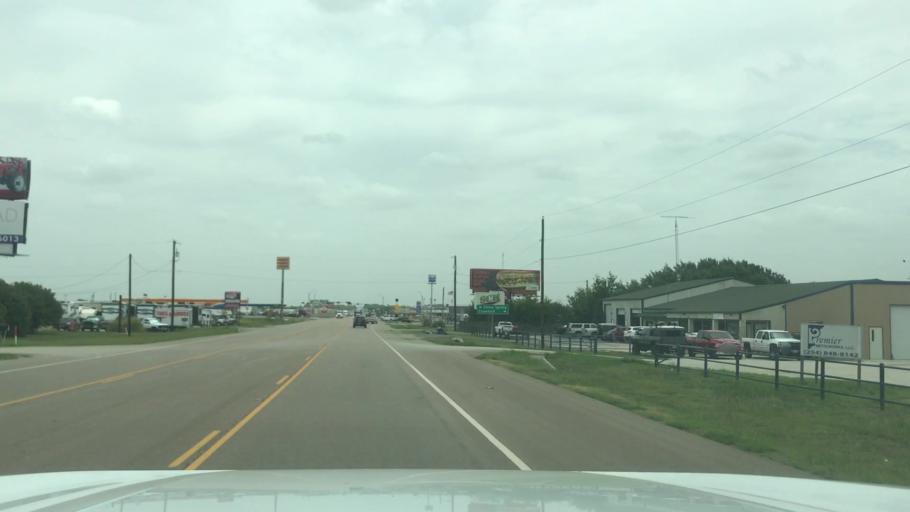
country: US
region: Texas
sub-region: McLennan County
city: Woodway
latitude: 31.5827
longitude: -97.3088
